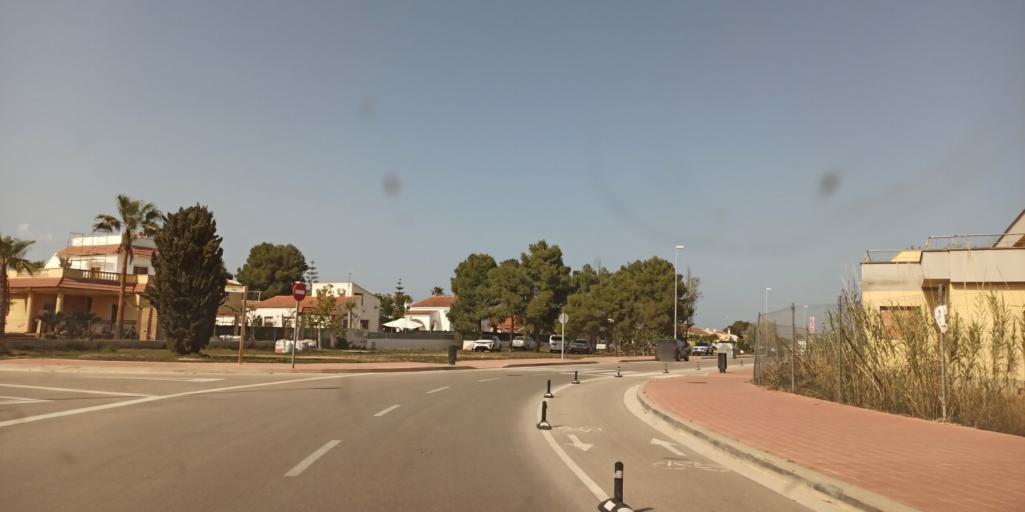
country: ES
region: Catalonia
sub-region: Provincia de Tarragona
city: Deltebre
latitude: 40.7246
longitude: 0.8425
